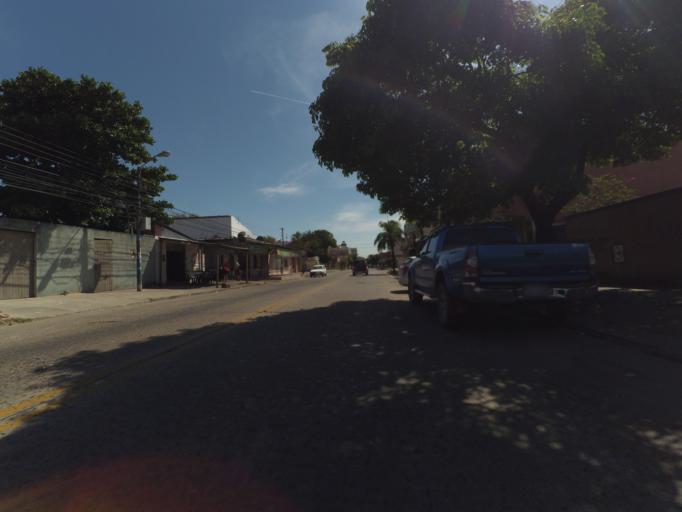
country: BO
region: Santa Cruz
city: Santa Cruz de la Sierra
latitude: -17.8034
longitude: -63.1930
